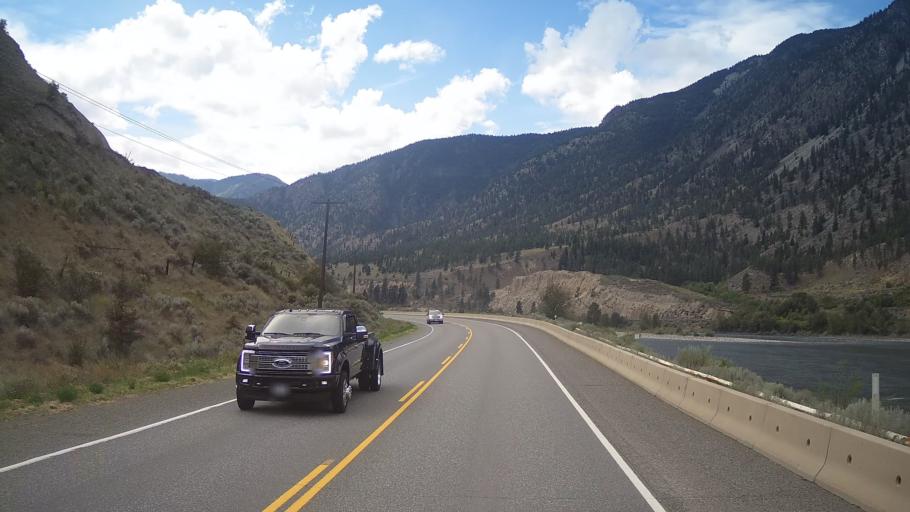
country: CA
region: British Columbia
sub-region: Thompson-Nicola Regional District
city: Ashcroft
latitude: 50.4065
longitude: -121.3707
